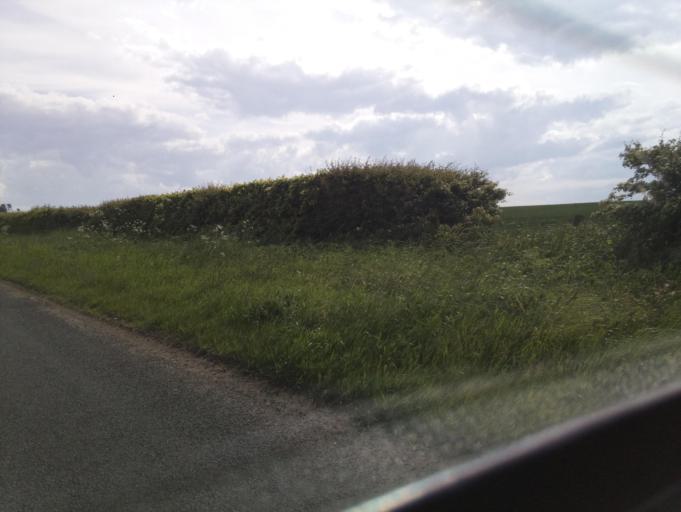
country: GB
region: England
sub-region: Northumberland
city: Alnwick
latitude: 55.4457
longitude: -1.7103
